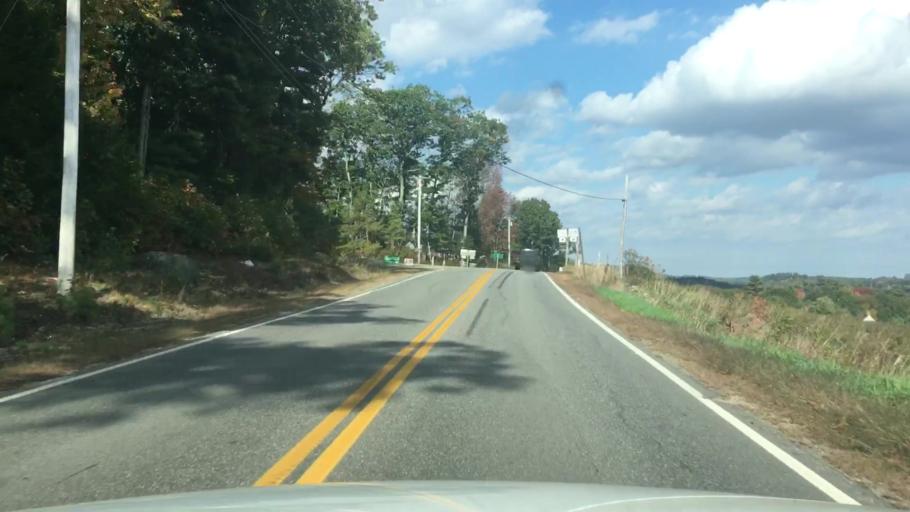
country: US
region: Maine
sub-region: Knox County
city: Appleton
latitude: 44.2624
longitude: -69.2749
